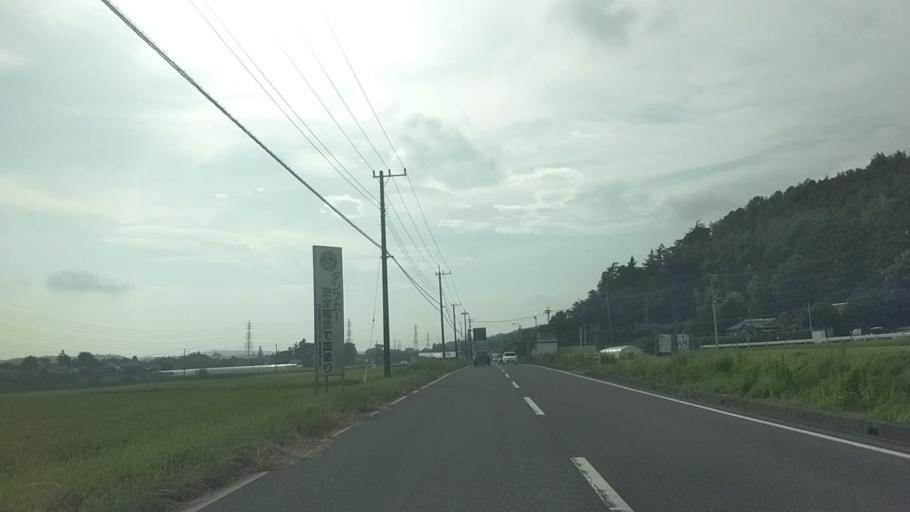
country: JP
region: Chiba
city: Kisarazu
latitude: 35.3098
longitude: 139.9719
